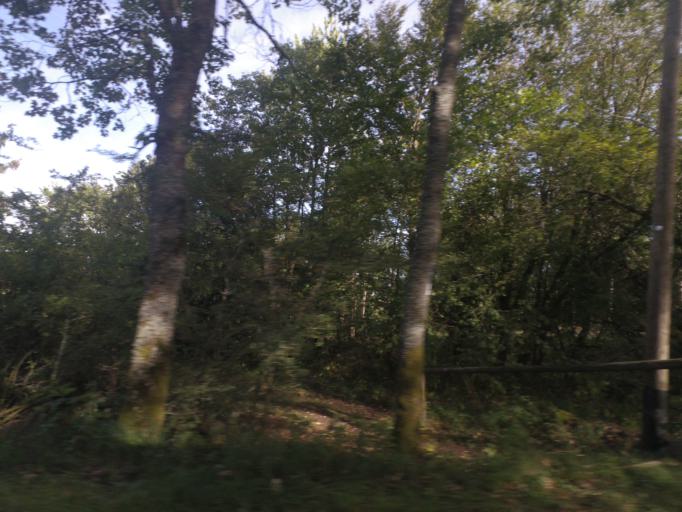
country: DE
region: Bavaria
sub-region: Regierungsbezirk Unterfranken
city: Hausen
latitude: 50.4989
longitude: 10.1103
